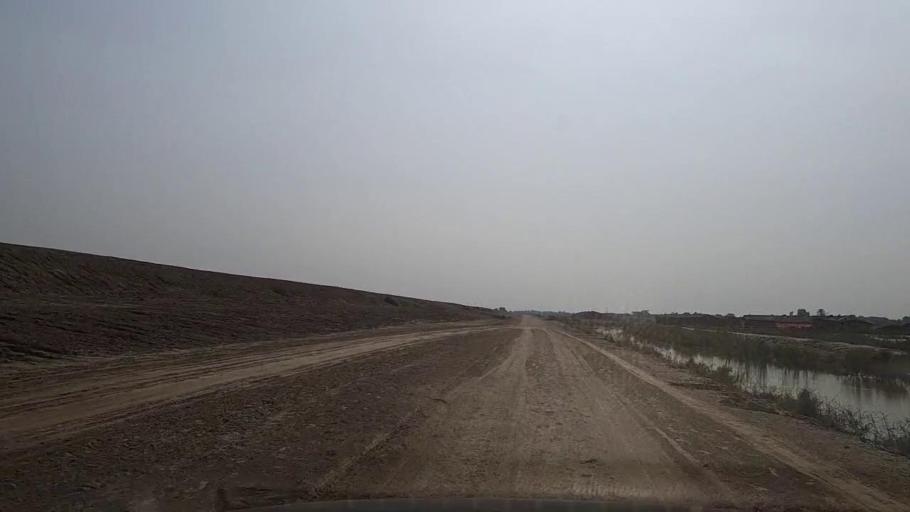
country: PK
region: Sindh
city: Thatta
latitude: 24.5691
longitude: 67.9133
